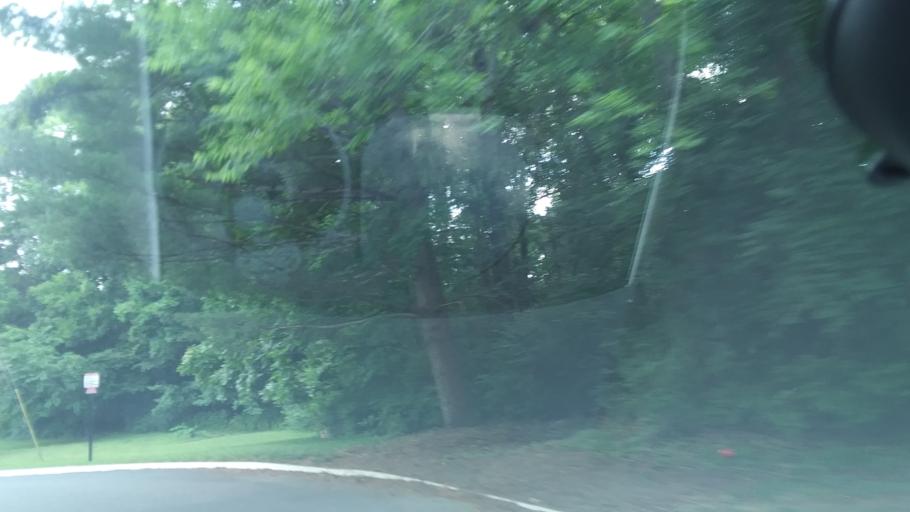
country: US
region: Tennessee
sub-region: Rutherford County
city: La Vergne
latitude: 36.0974
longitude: -86.6607
